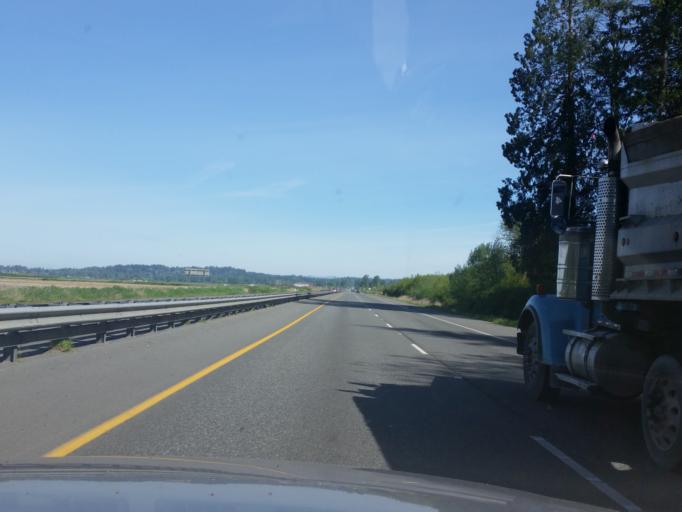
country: US
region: Washington
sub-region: Snohomish County
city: Cathcart
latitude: 47.8800
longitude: -122.1098
